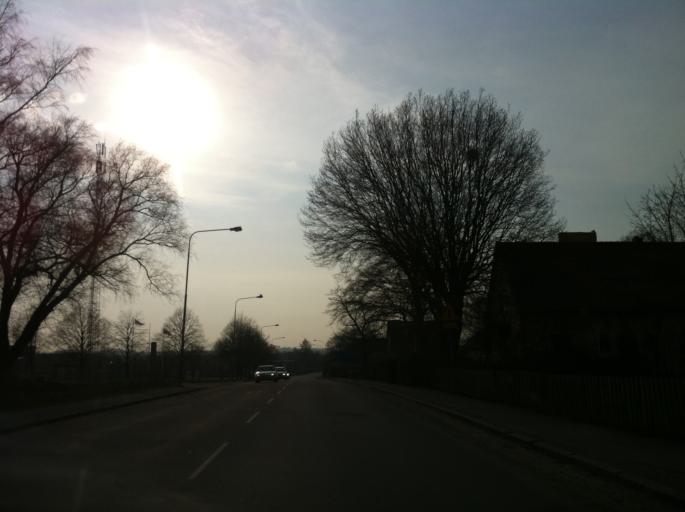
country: SE
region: Skane
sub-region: Svalovs Kommun
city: Svaloev
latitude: 55.9138
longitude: 13.1689
